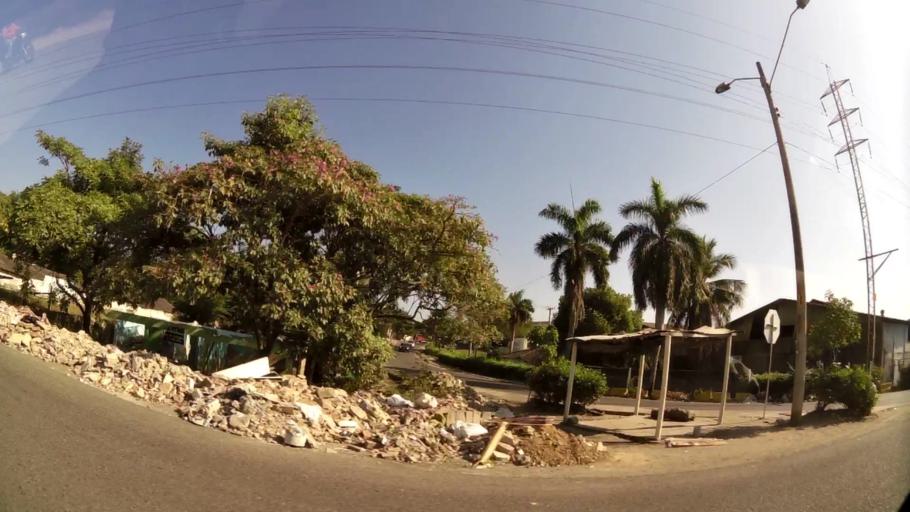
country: CO
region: Bolivar
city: Cartagena
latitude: 10.3861
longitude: -75.5091
